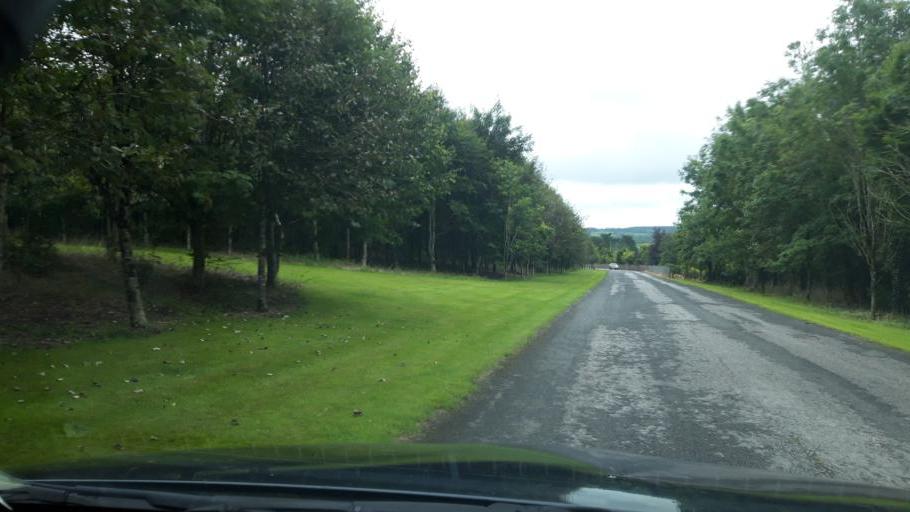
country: IE
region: Munster
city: Cahir
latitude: 52.1864
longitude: -7.8554
